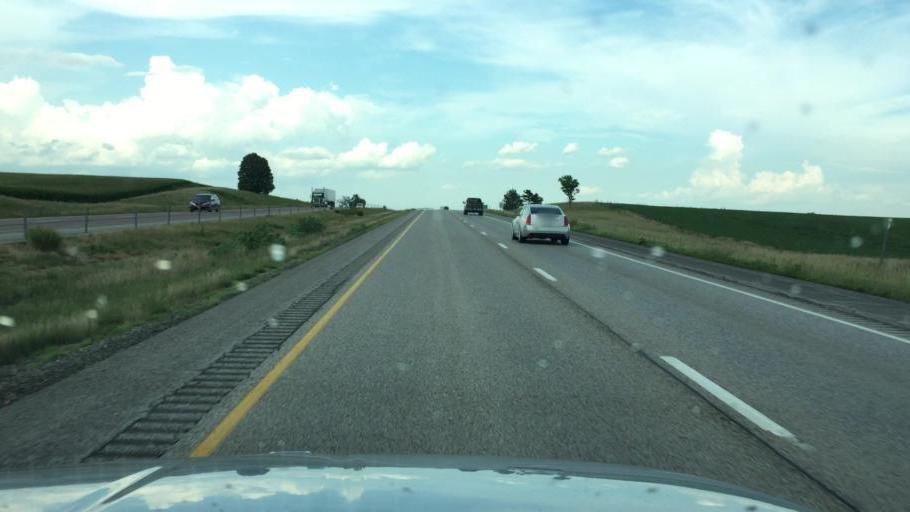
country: US
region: Iowa
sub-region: Iowa County
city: Marengo
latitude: 41.6961
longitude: -92.1905
